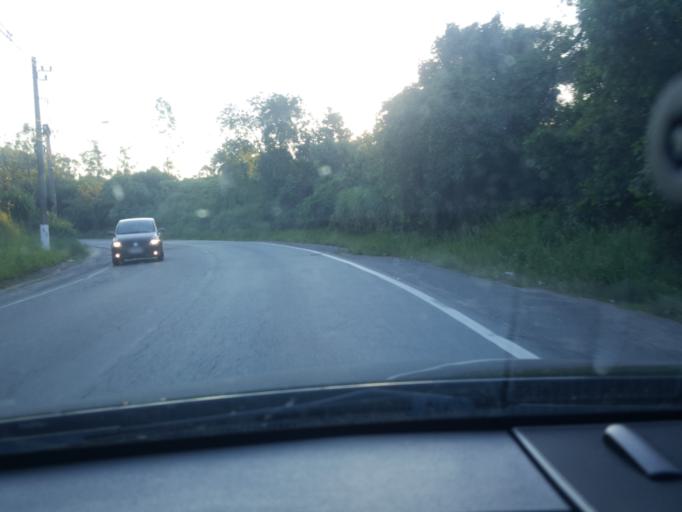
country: BR
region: Sao Paulo
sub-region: Cajamar
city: Cajamar
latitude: -23.3957
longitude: -46.8670
